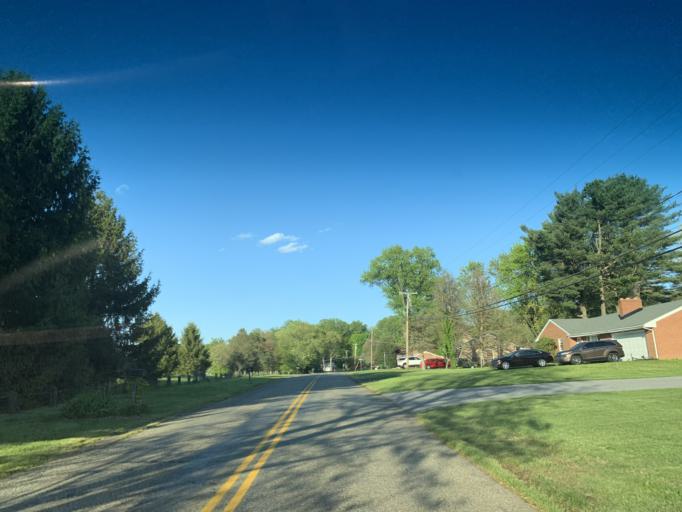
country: US
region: Maryland
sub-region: Harford County
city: Aberdeen
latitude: 39.5401
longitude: -76.1822
